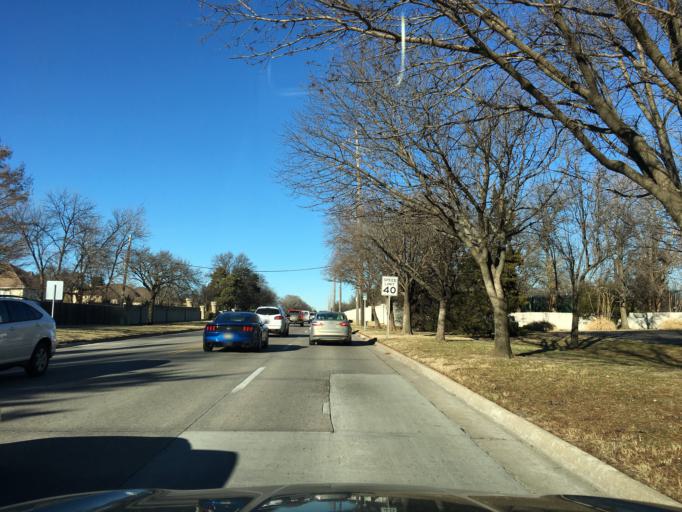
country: US
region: Kansas
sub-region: Sedgwick County
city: Bellaire
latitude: 37.7005
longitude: -97.2446
